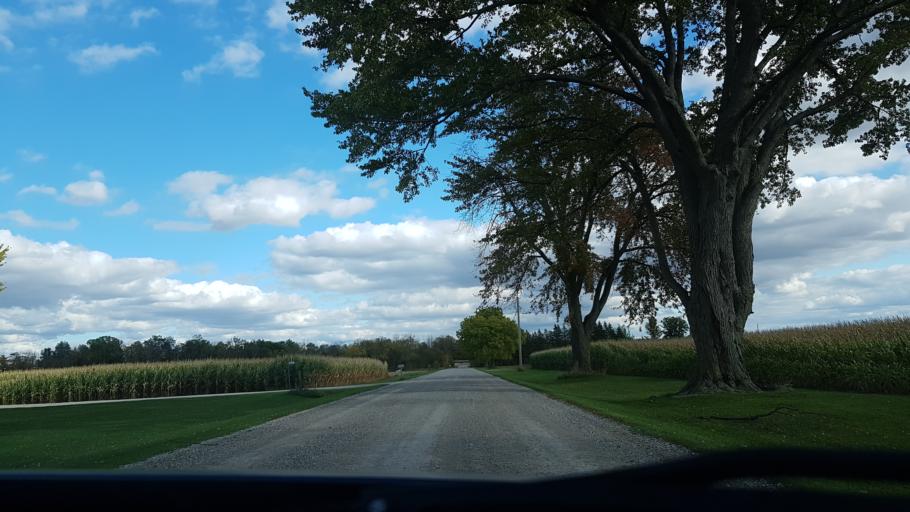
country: CA
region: Ontario
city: South Huron
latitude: 43.1073
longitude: -81.6155
